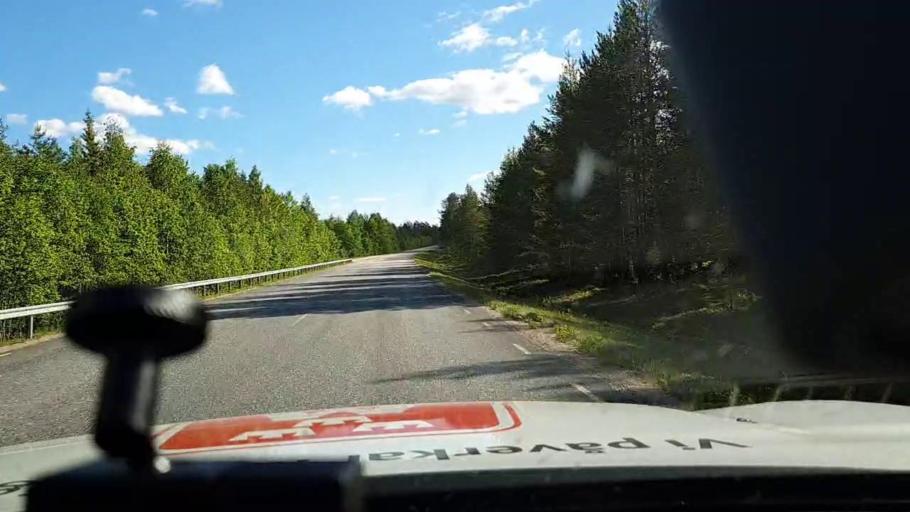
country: SE
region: Norrbotten
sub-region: Overtornea Kommun
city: OEvertornea
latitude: 66.3443
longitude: 23.6482
